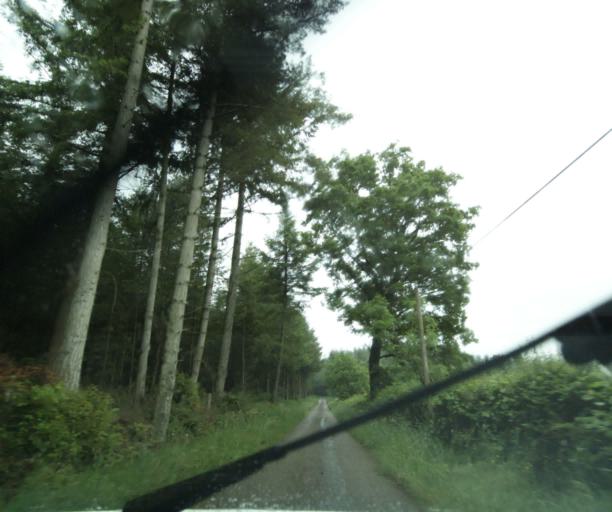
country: FR
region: Bourgogne
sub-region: Departement de Saone-et-Loire
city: La Clayette
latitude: 46.3690
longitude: 4.3669
